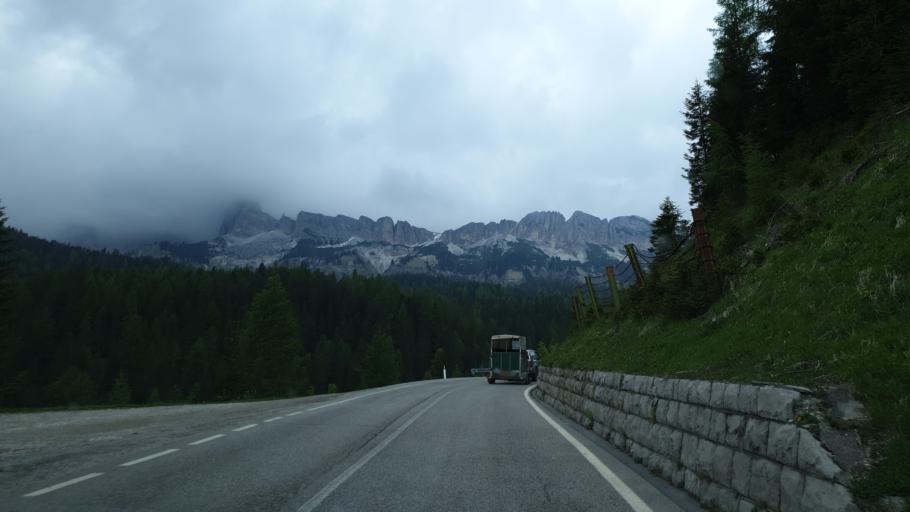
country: IT
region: Veneto
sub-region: Provincia di Belluno
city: San Vito
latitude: 46.5574
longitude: 12.2461
